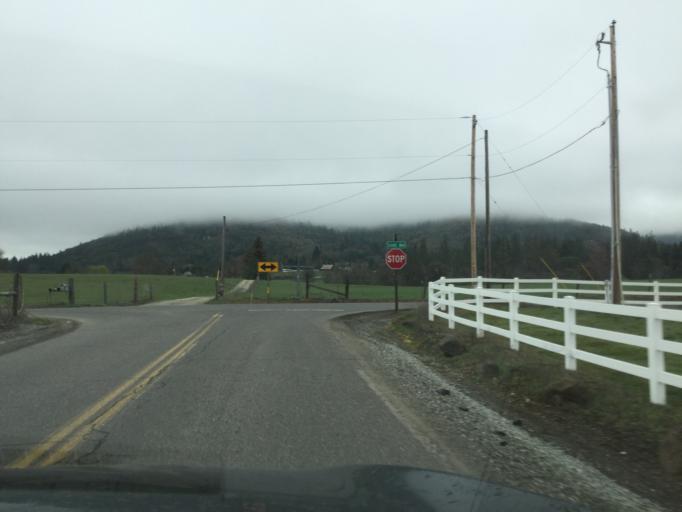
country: US
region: Oregon
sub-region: Jackson County
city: Central Point
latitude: 42.3907
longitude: -122.9686
